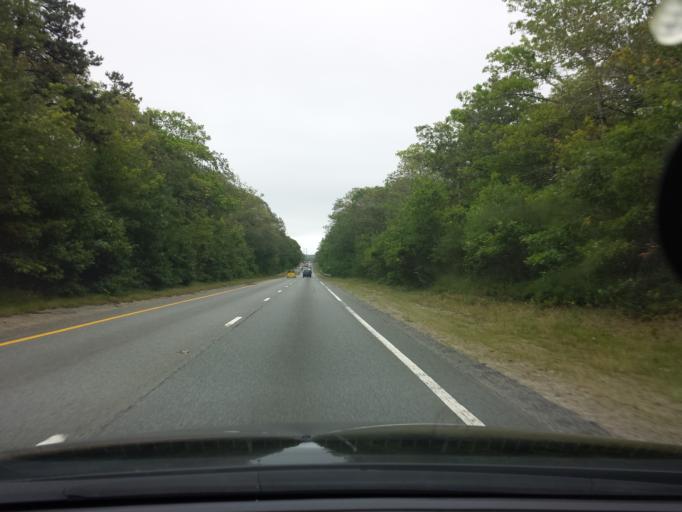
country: US
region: Massachusetts
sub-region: Barnstable County
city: West Barnstable
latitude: 41.7003
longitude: -70.3929
